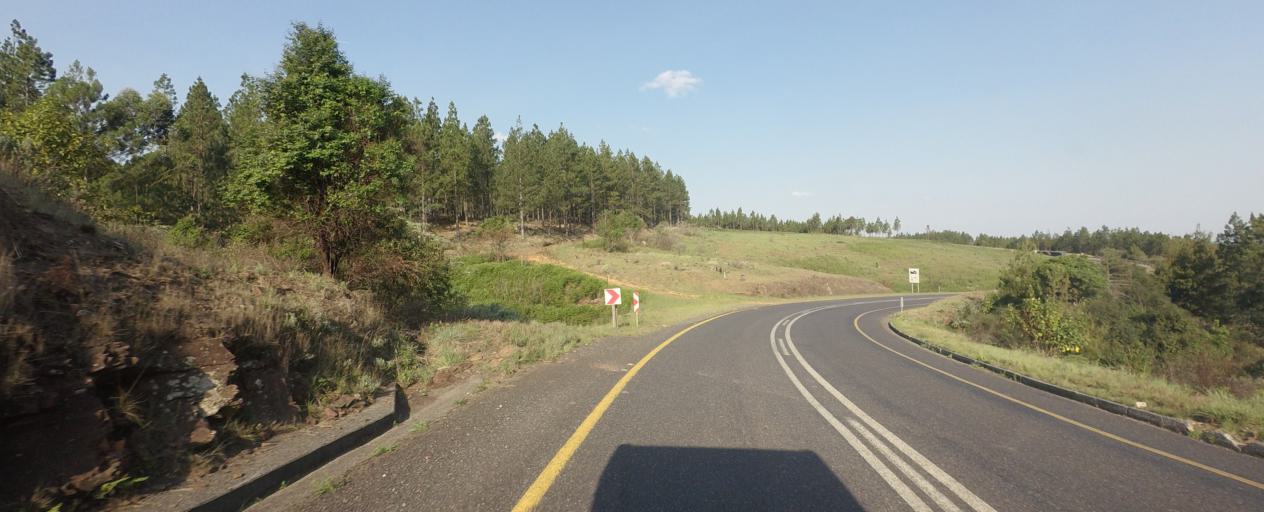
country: ZA
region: Mpumalanga
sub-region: Ehlanzeni District
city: Lydenburg
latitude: -25.1814
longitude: 30.7003
